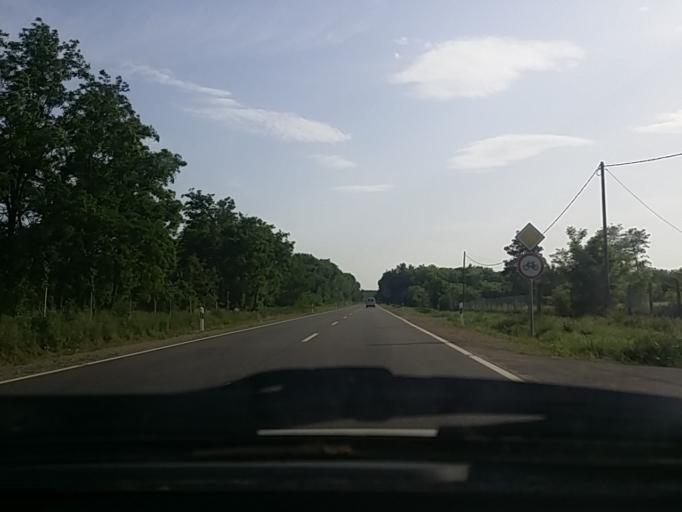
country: HU
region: Jasz-Nagykun-Szolnok
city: Jaszbereny
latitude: 47.4819
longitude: 19.8739
